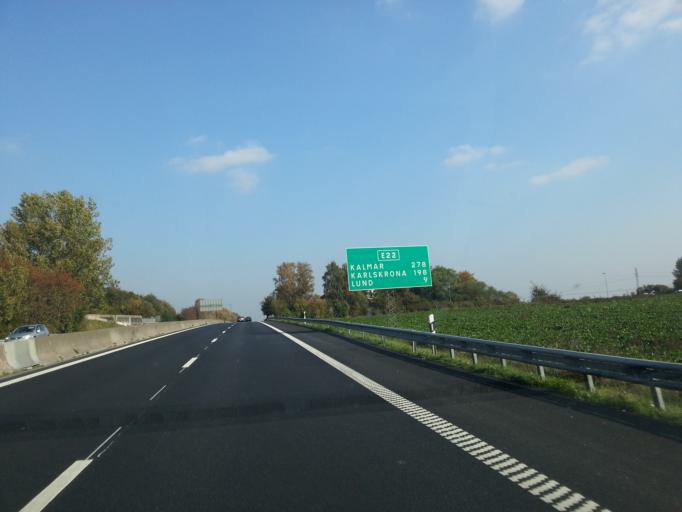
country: SE
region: Skane
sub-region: Staffanstorps Kommun
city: Hjaerup
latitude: 55.6468
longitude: 13.1169
